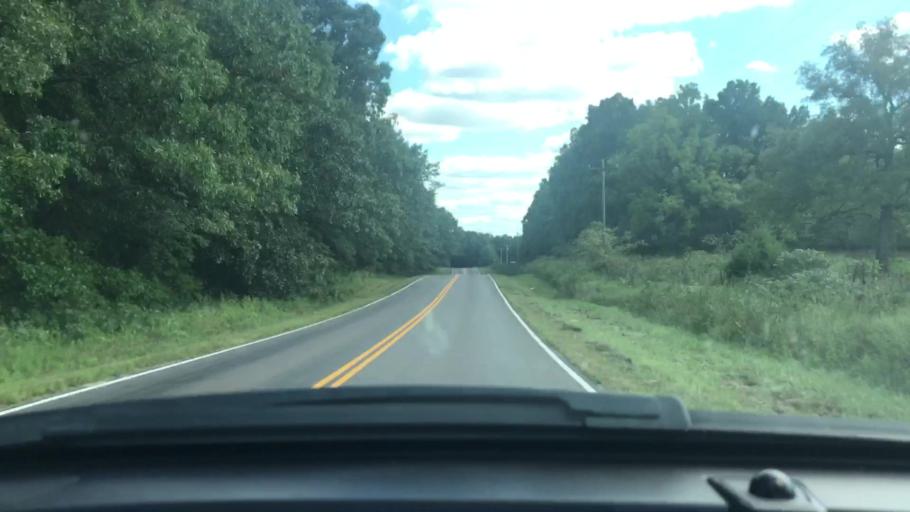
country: US
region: Missouri
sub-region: Wright County
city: Hartville
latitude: 37.3583
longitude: -92.3426
